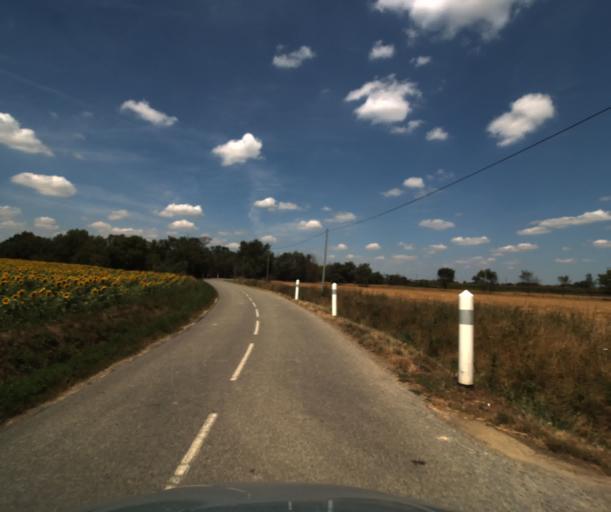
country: FR
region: Midi-Pyrenees
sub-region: Departement de la Haute-Garonne
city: Saint-Lys
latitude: 43.4924
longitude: 1.1792
